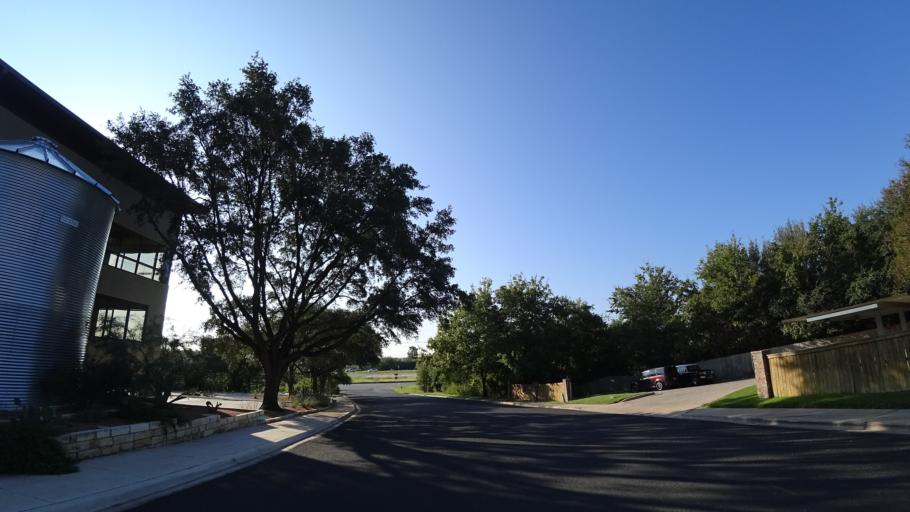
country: US
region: Texas
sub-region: Travis County
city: Rollingwood
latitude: 30.2598
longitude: -97.7982
